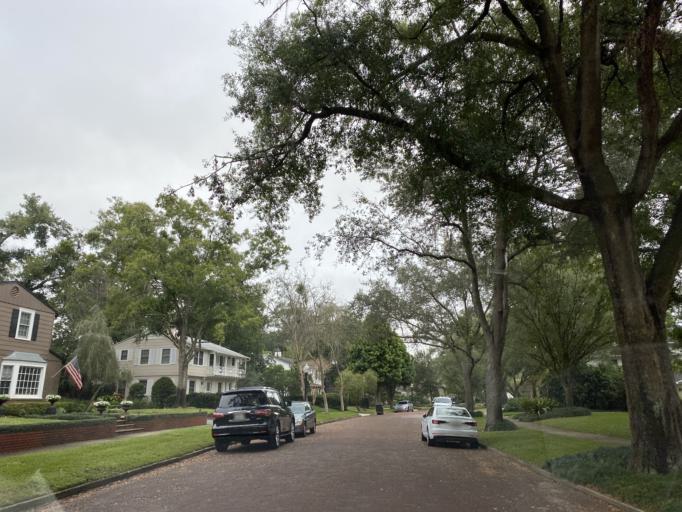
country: US
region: Florida
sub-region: Orange County
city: Orlando
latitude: 28.5619
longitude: -81.3943
